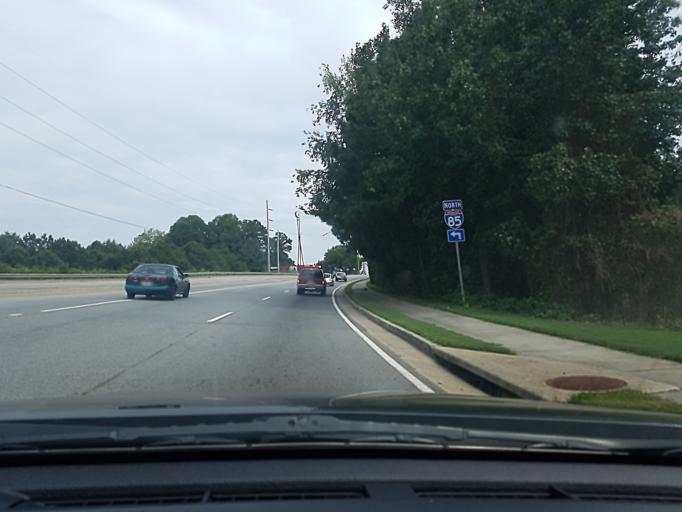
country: US
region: Georgia
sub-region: Gwinnett County
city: Norcross
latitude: 33.9380
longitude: -84.1622
